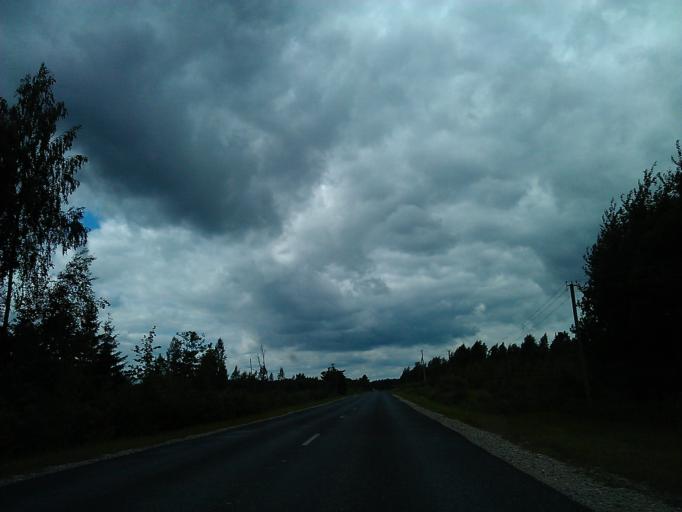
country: LV
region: Talsu Rajons
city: Stende
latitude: 57.0916
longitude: 22.3693
